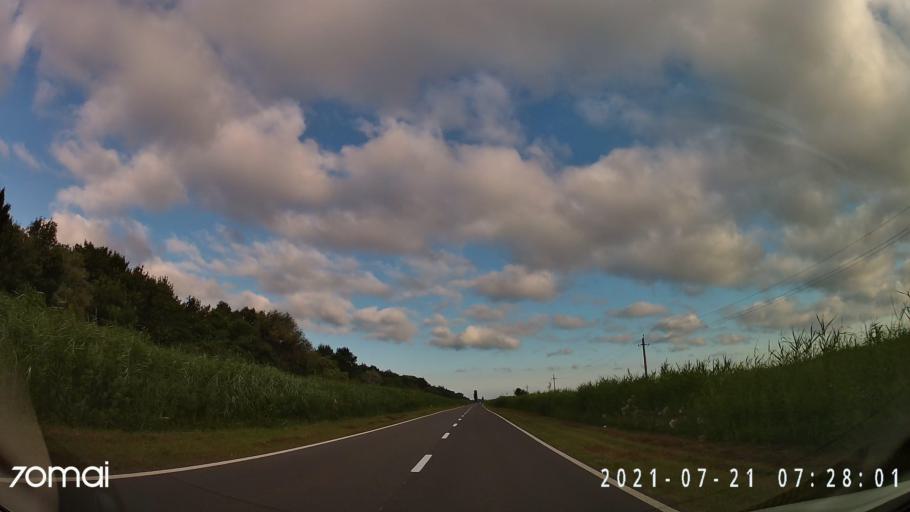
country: RO
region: Tulcea
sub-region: Oras Isaccea
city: Isaccea
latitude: 45.3078
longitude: 28.4028
